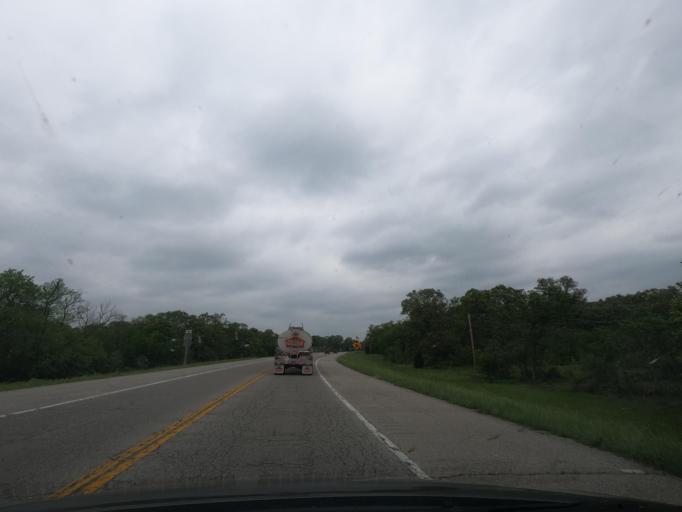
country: US
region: Kansas
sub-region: Cherokee County
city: Galena
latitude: 37.0215
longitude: -94.6413
